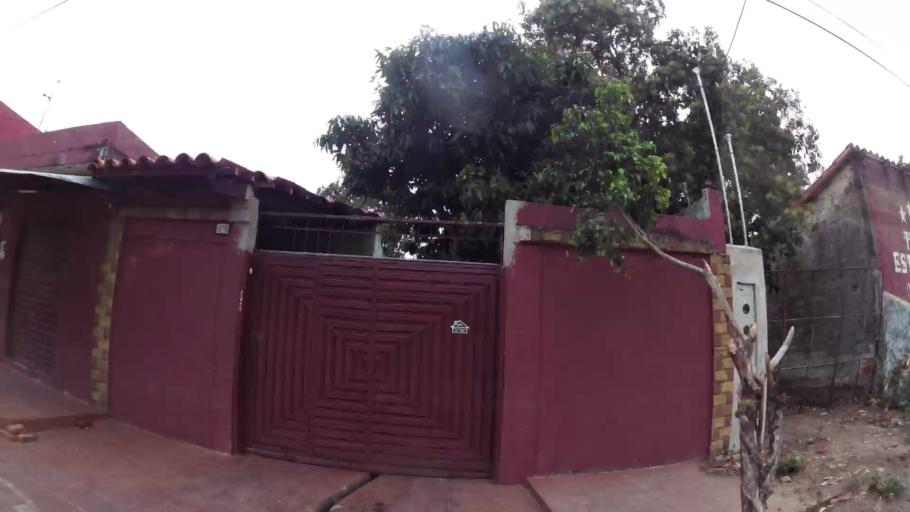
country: BO
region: Santa Cruz
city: Santa Cruz de la Sierra
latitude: -17.7742
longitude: -63.2126
